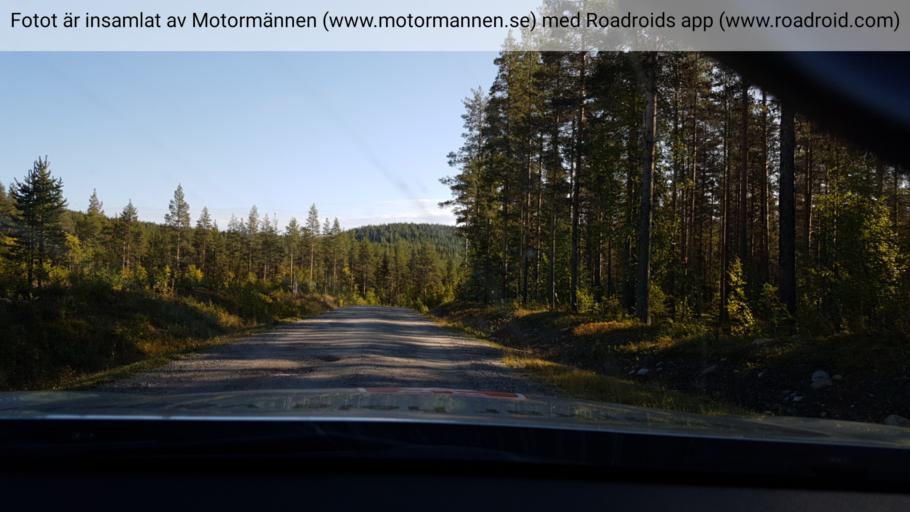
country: SE
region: Vaesterbotten
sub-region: Norsjo Kommun
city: Norsjoe
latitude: 64.6983
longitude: 19.4876
